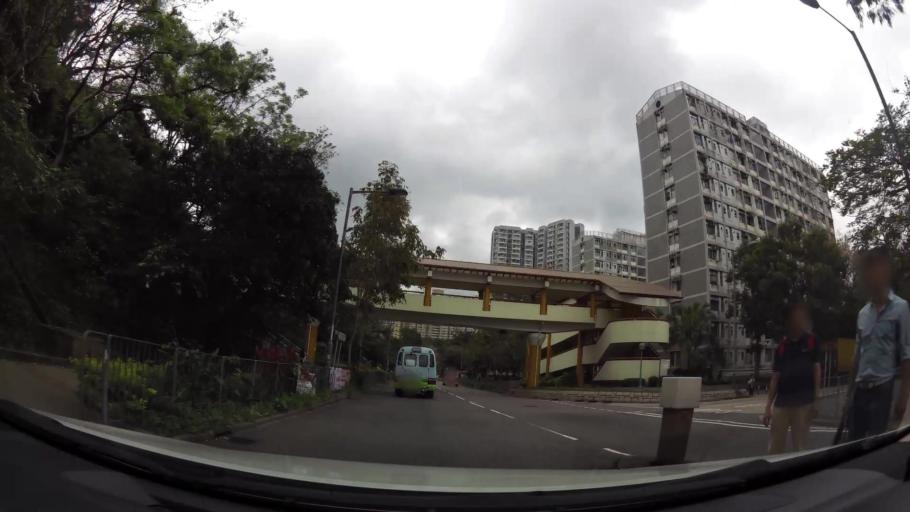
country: HK
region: Wong Tai Sin
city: Wong Tai Sin
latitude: 22.3346
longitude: 114.1911
